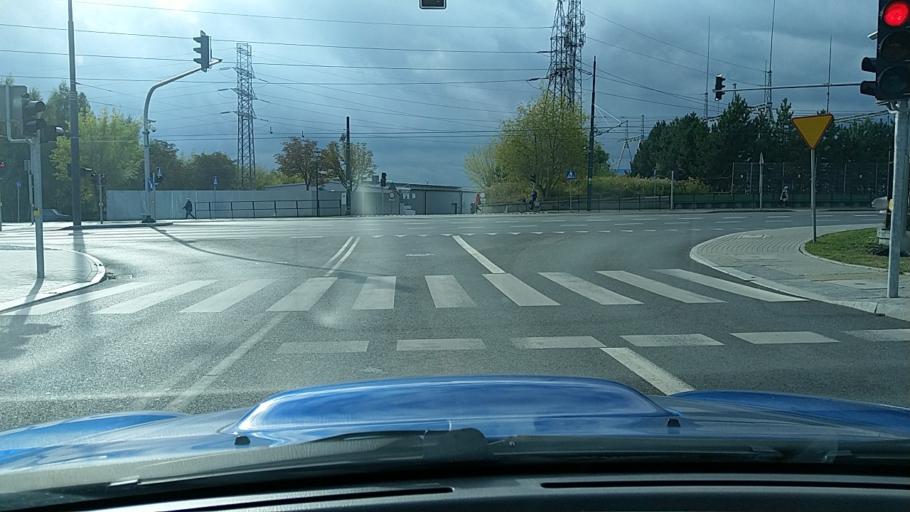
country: PL
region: Warmian-Masurian Voivodeship
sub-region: Powiat olsztynski
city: Olsztyn
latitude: 53.7625
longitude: 20.4872
